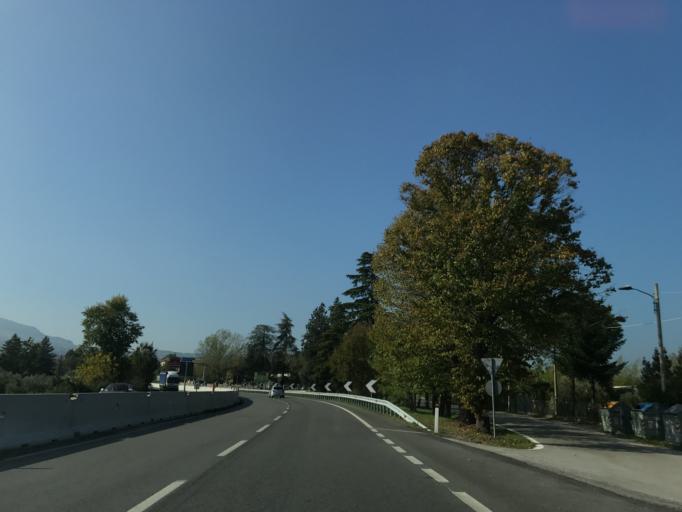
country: SM
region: Serravalle
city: Serravalle
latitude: 43.9884
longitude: 12.4983
